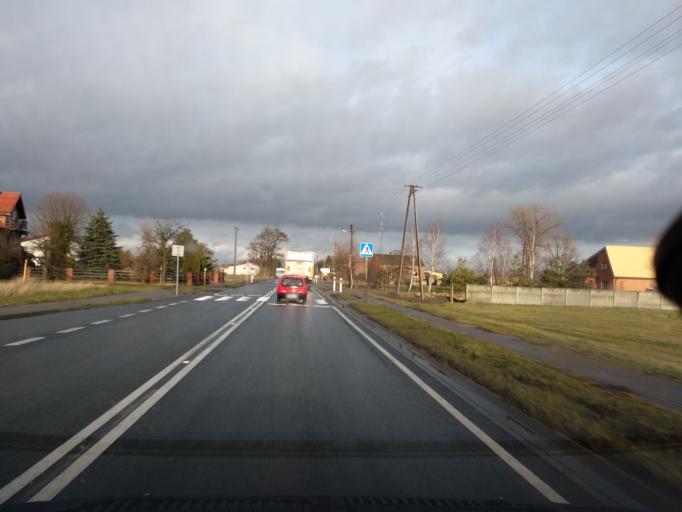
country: PL
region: Greater Poland Voivodeship
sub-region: Powiat koninski
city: Rychwal
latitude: 52.1182
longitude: 18.1684
